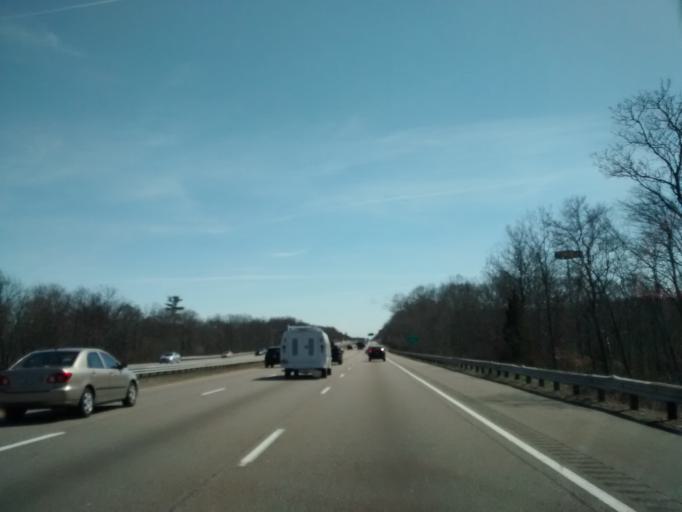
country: US
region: Massachusetts
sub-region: Norfolk County
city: Avon
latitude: 42.1416
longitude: -71.0659
